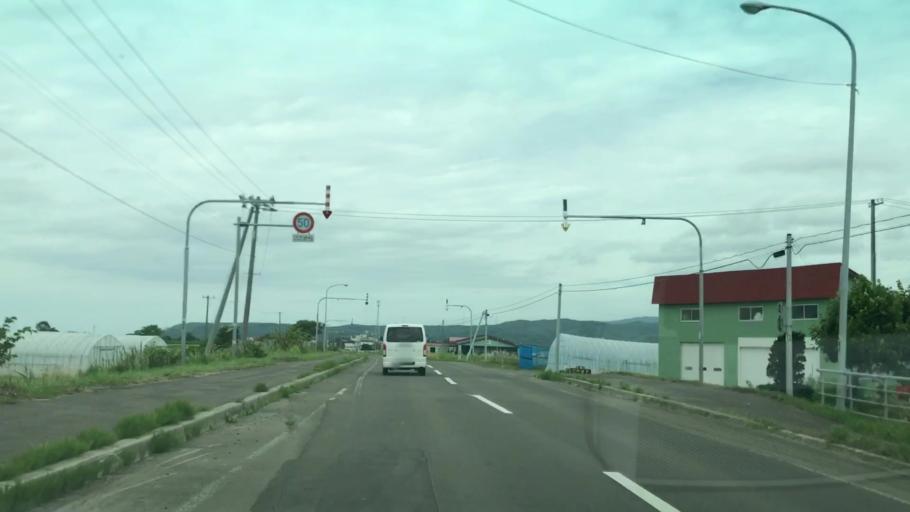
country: JP
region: Hokkaido
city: Iwanai
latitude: 43.0109
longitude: 140.5758
